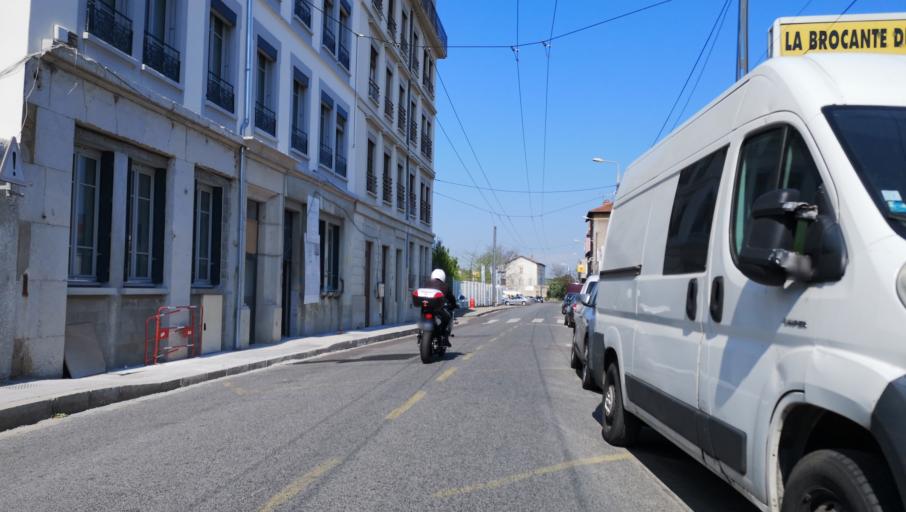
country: FR
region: Rhone-Alpes
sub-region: Departement du Rhone
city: Ecully
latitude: 45.7793
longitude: 4.7990
